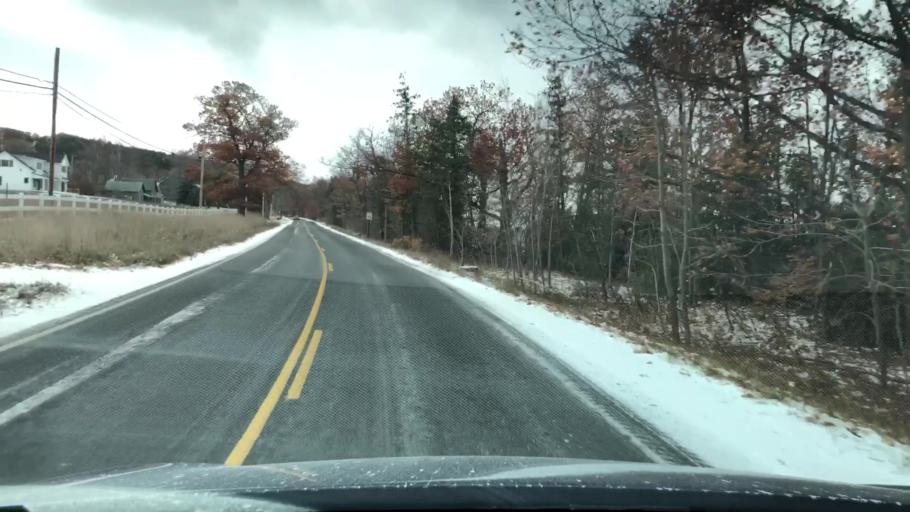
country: US
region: Michigan
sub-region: Grand Traverse County
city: Traverse City
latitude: 44.8089
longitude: -85.5810
